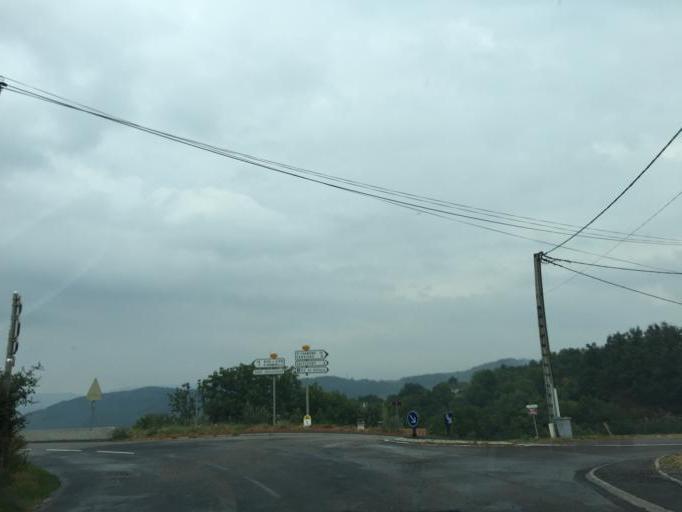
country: FR
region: Rhone-Alpes
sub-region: Departement de la Loire
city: Saint-Christo-en-Jarez
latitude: 45.5354
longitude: 4.4874
